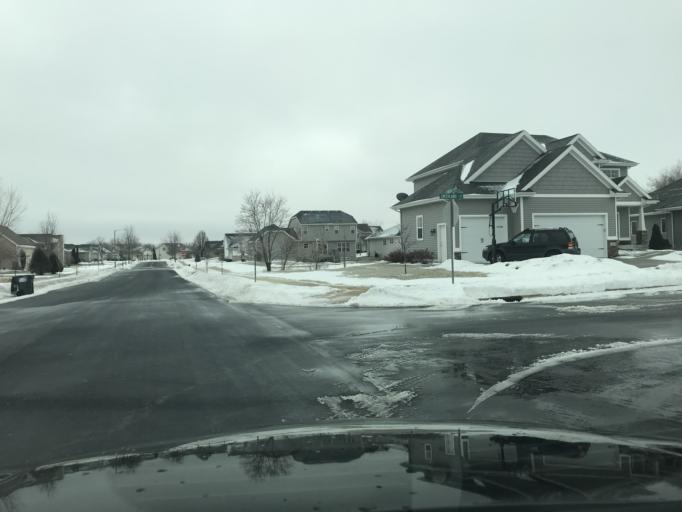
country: US
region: Wisconsin
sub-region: Dane County
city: Cottage Grove
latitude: 43.0944
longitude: -89.2126
